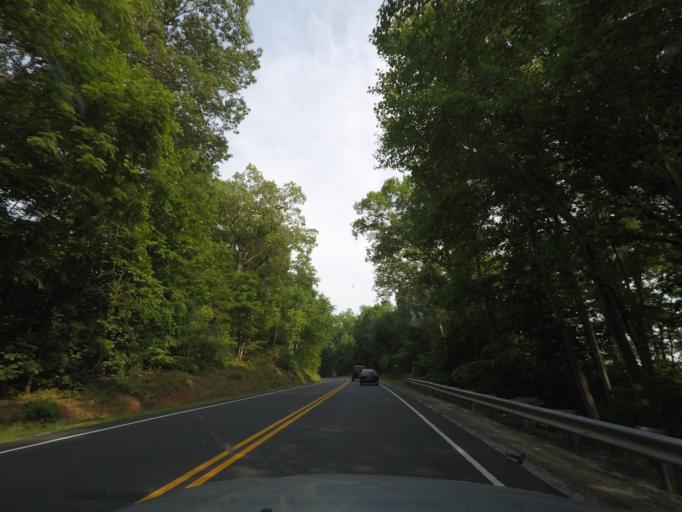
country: US
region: Virginia
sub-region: Prince Edward County
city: Hampden Sydney
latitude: 37.2062
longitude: -78.4423
